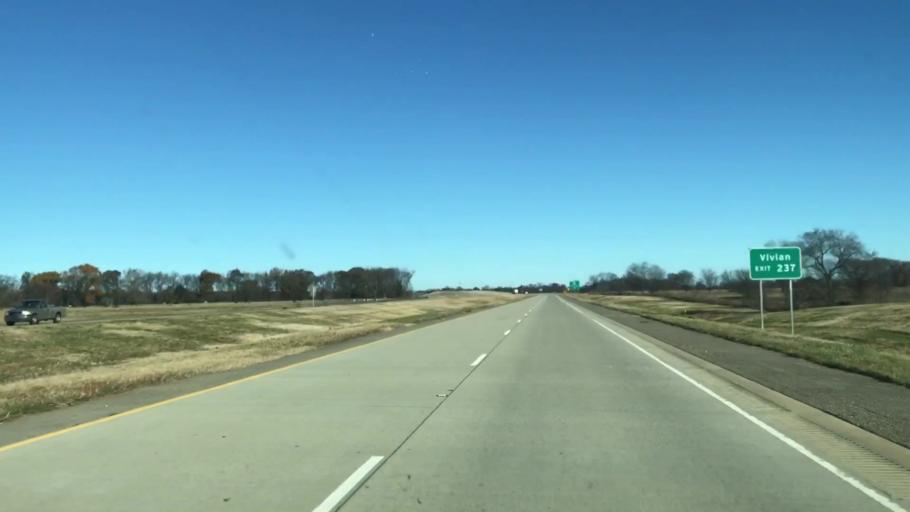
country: US
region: Louisiana
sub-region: Caddo Parish
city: Vivian
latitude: 32.8854
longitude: -93.8600
